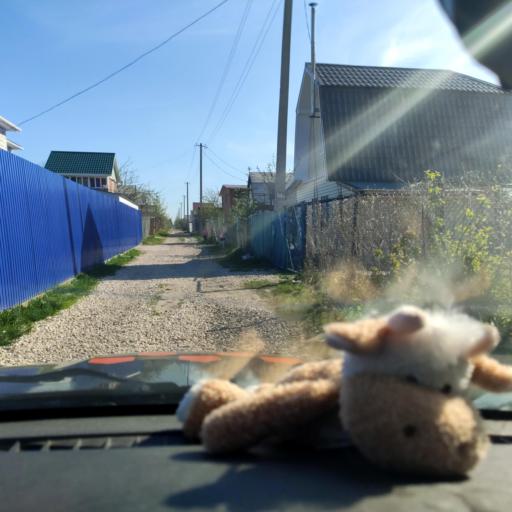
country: RU
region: Samara
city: Tol'yatti
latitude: 53.6025
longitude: 49.2661
